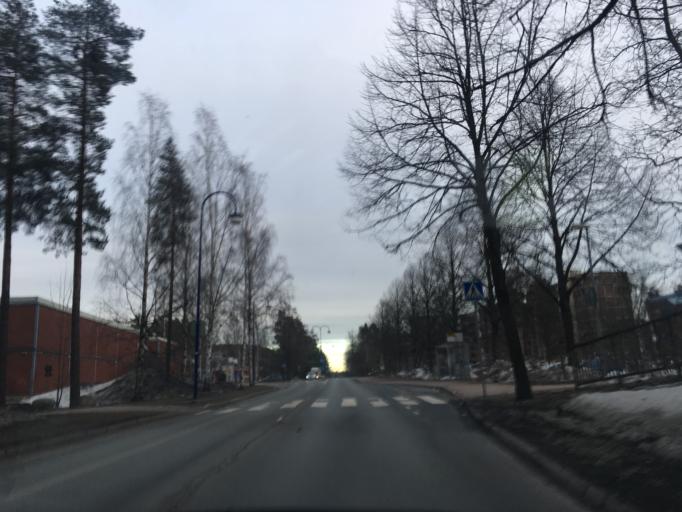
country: FI
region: Uusimaa
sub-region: Helsinki
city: Vantaa
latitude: 60.3245
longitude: 25.0744
